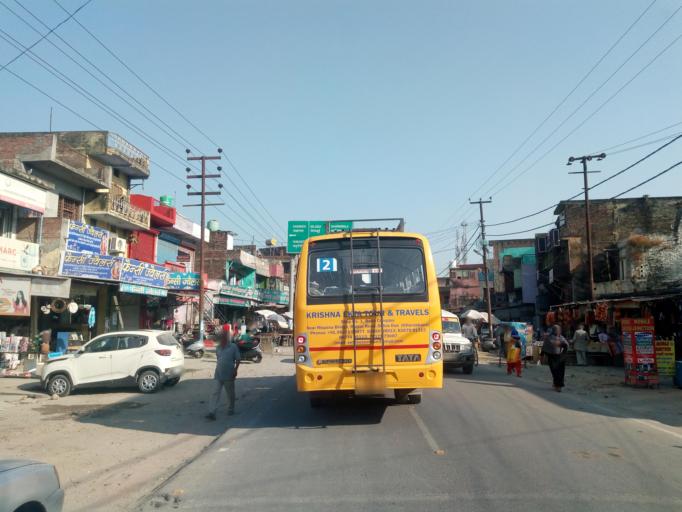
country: IN
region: Uttarakhand
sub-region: Dehradun
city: Harbatpur
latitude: 30.4395
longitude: 77.7359
